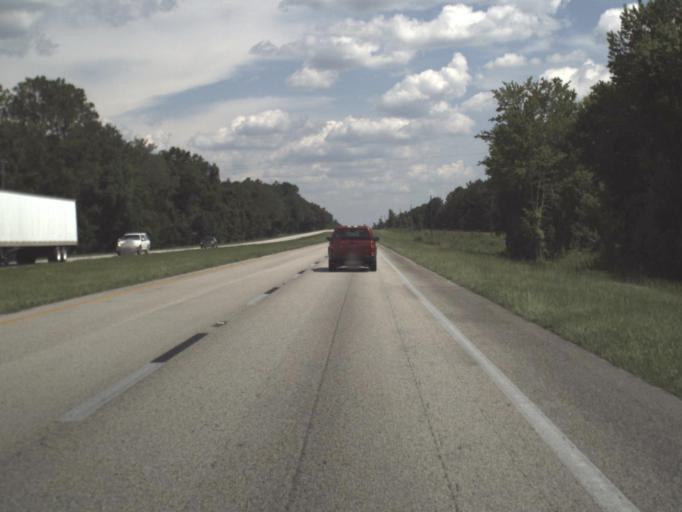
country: US
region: Florida
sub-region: Alachua County
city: Waldo
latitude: 29.7037
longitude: -82.1344
